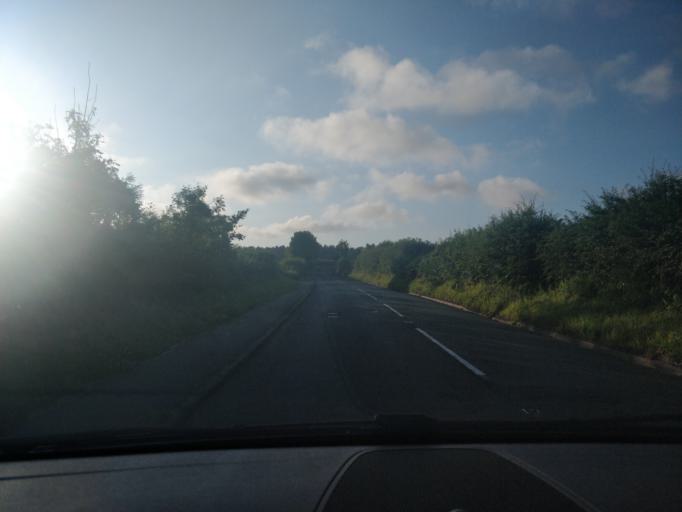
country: GB
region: England
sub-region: Lancashire
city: Appley Bridge
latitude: 53.5482
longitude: -2.7387
